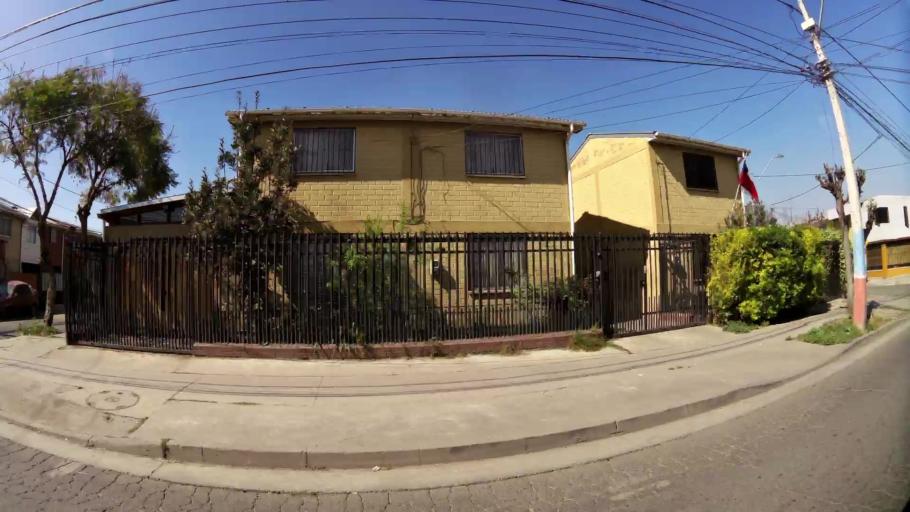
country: CL
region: Santiago Metropolitan
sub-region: Provincia de Santiago
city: Lo Prado
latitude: -33.3513
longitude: -70.7477
